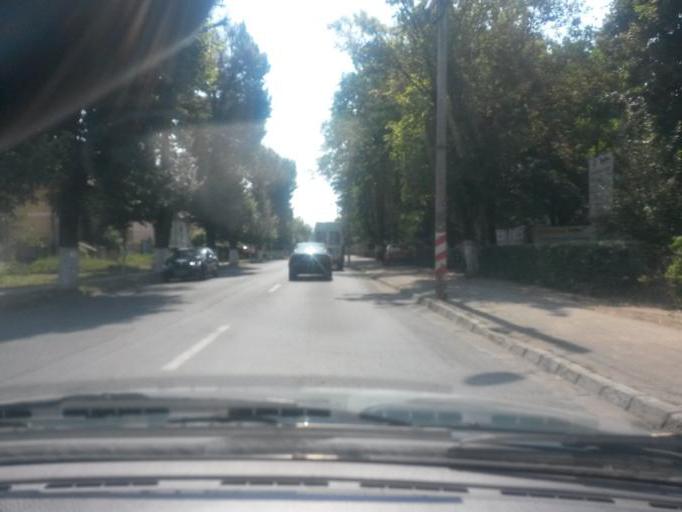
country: RO
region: Mures
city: Targu-Mures
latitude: 46.5496
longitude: 24.5731
